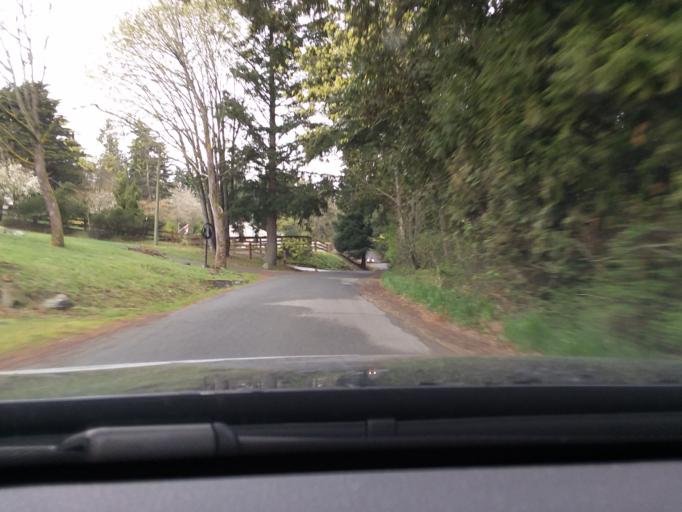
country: CA
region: British Columbia
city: Victoria
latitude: 48.5489
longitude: -123.3900
